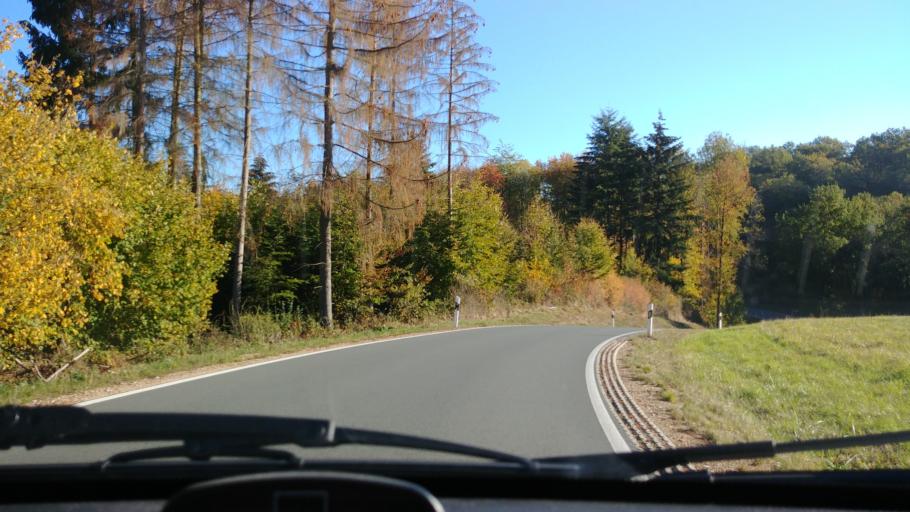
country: DE
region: Rheinland-Pfalz
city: Lollschied
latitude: 50.2562
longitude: 7.8779
